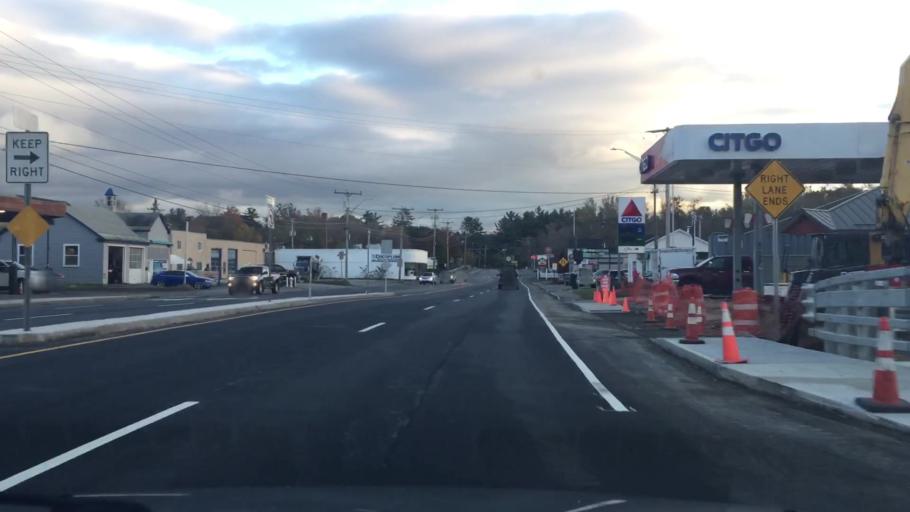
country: US
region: New Hampshire
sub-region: Cheshire County
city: Keene
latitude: 42.9210
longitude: -72.2757
